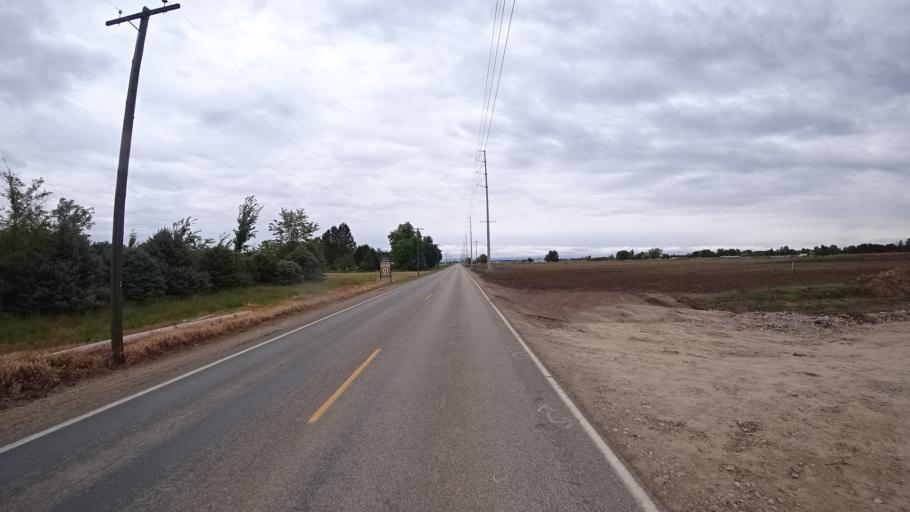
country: US
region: Idaho
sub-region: Ada County
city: Star
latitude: 43.6486
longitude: -116.4833
